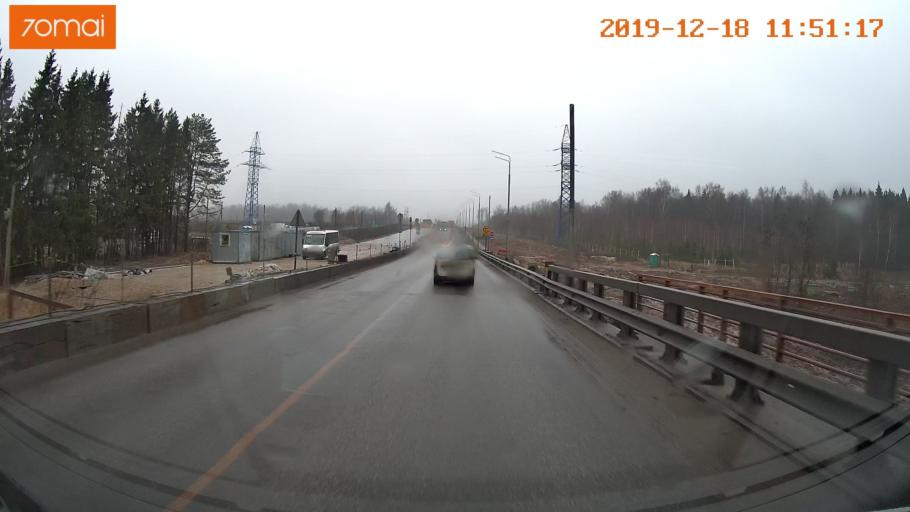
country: RU
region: Moskovskaya
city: Yershovo
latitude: 55.7923
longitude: 36.9219
